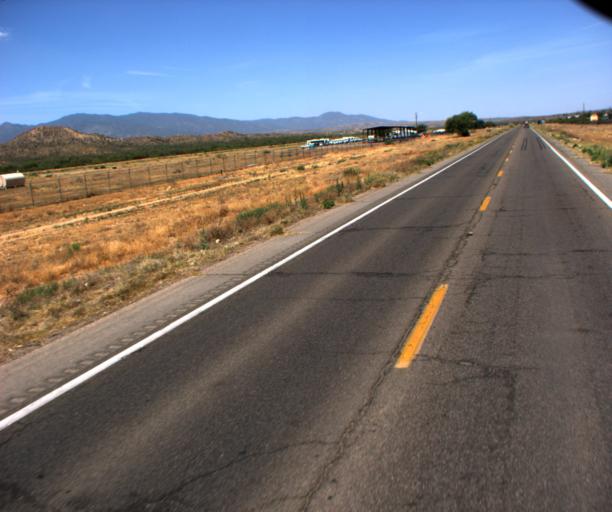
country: US
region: Arizona
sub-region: Gila County
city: Globe
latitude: 33.3530
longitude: -110.6553
